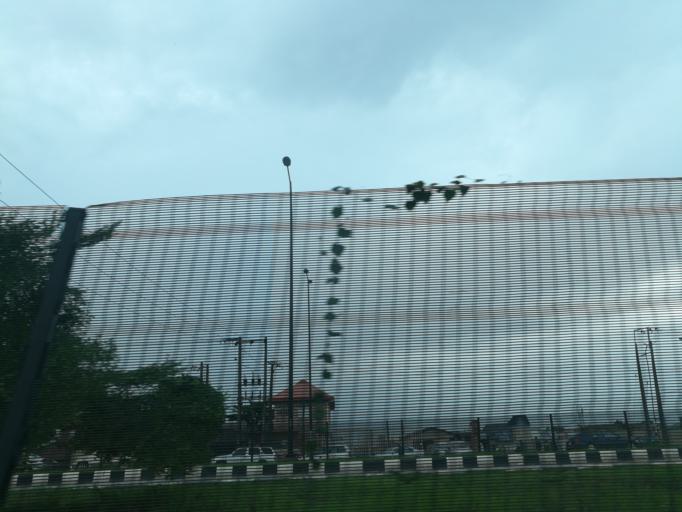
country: NG
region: Lagos
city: Ojota
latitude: 6.6073
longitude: 3.4083
